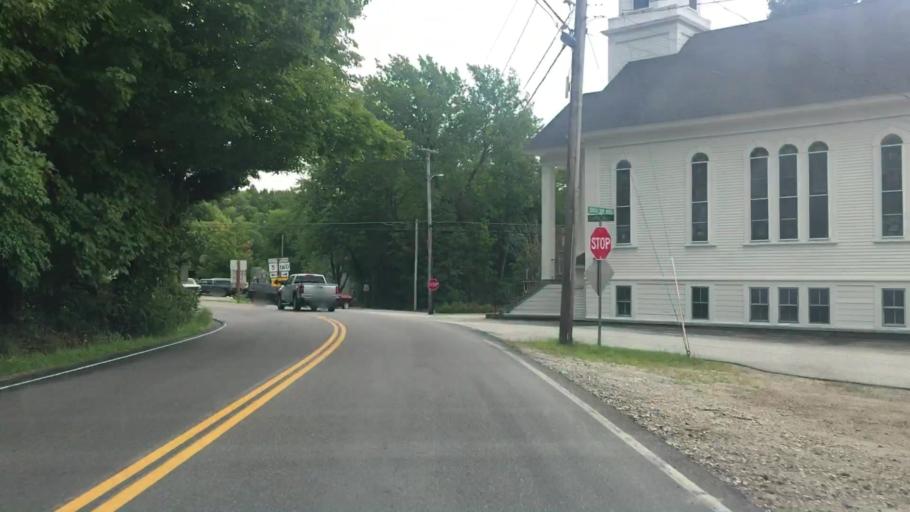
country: US
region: Maine
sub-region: York County
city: Limerick
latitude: 43.6897
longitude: -70.7964
